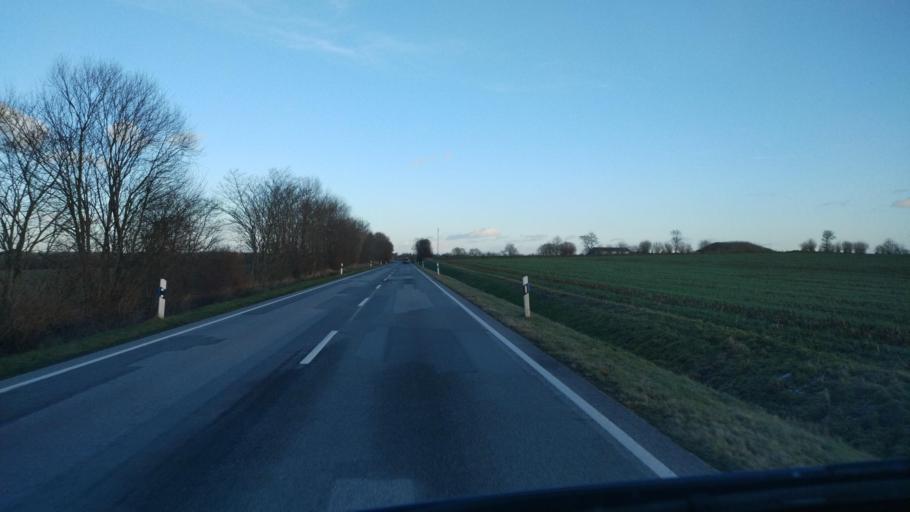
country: DE
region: Schleswig-Holstein
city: Wittbek
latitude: 54.4617
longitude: 9.1920
